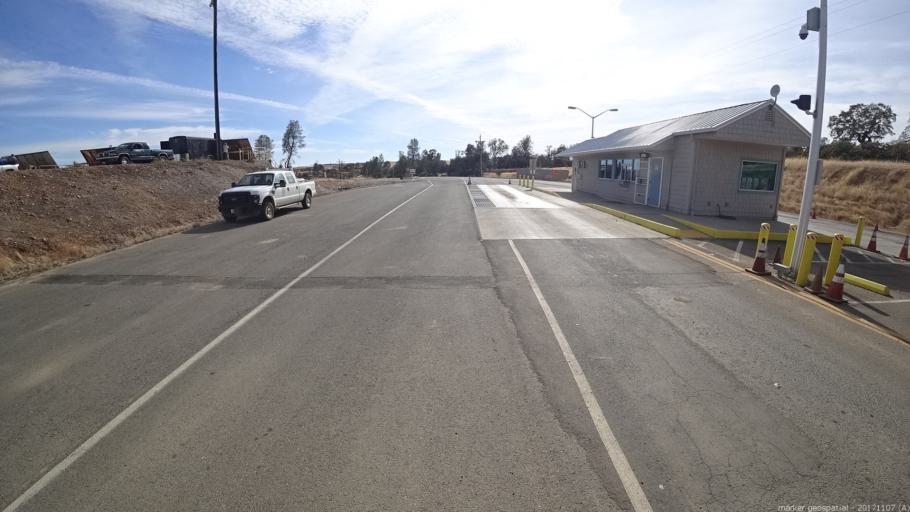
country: US
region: California
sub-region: Shasta County
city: Shasta
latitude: 40.4886
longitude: -122.5383
